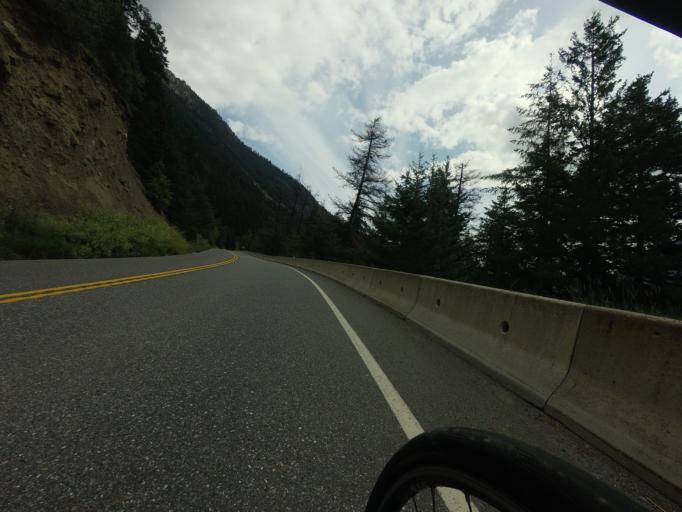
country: CA
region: British Columbia
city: Lillooet
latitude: 50.6458
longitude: -122.0225
